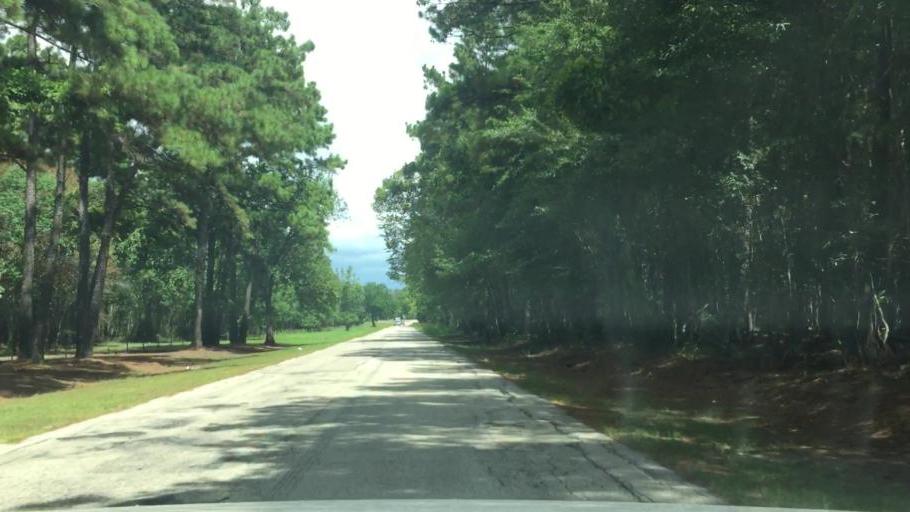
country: US
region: Texas
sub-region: Harris County
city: Jersey Village
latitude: 29.8132
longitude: -95.6222
